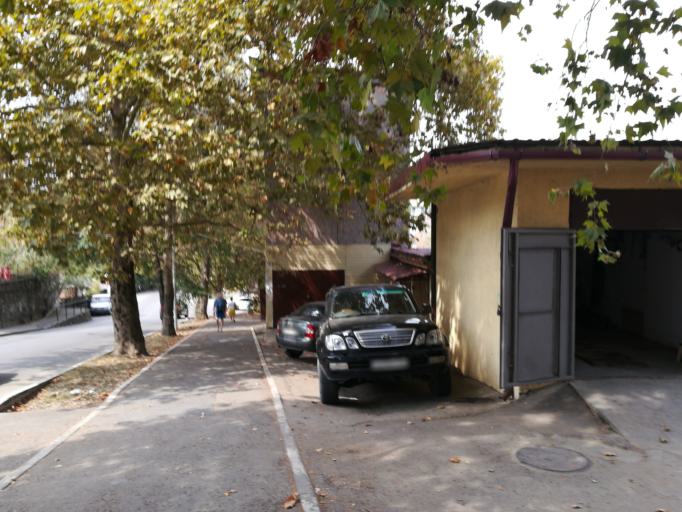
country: RU
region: Krasnodarskiy
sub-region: Sochi City
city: Sochi
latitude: 43.5946
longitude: 39.7358
